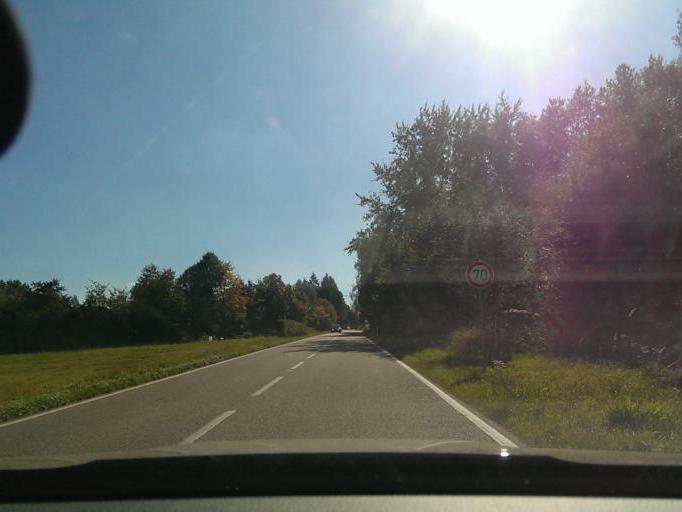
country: DE
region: Baden-Wuerttemberg
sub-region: Karlsruhe Region
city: Dobel
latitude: 48.8026
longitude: 8.4881
